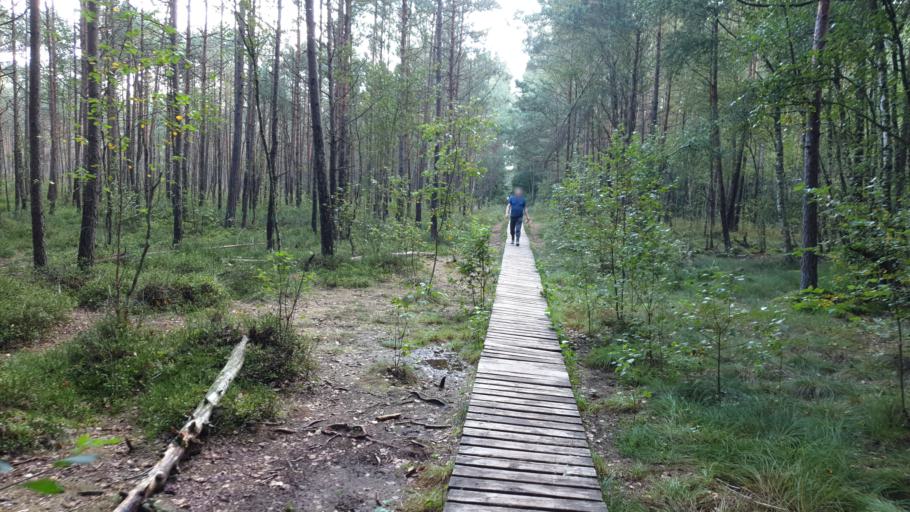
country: LT
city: Trakai
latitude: 54.6443
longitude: 24.9674
